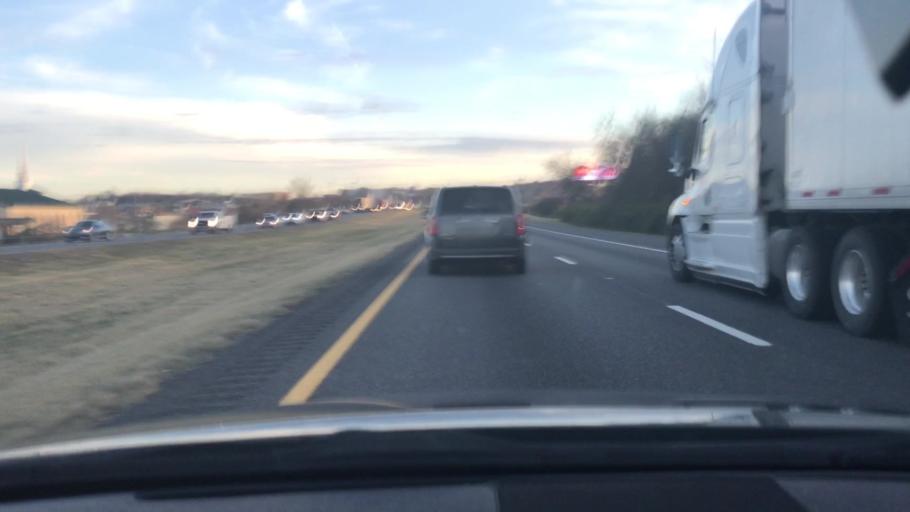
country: US
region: Tennessee
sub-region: Davidson County
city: Goodlettsville
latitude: 36.3288
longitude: -86.7076
